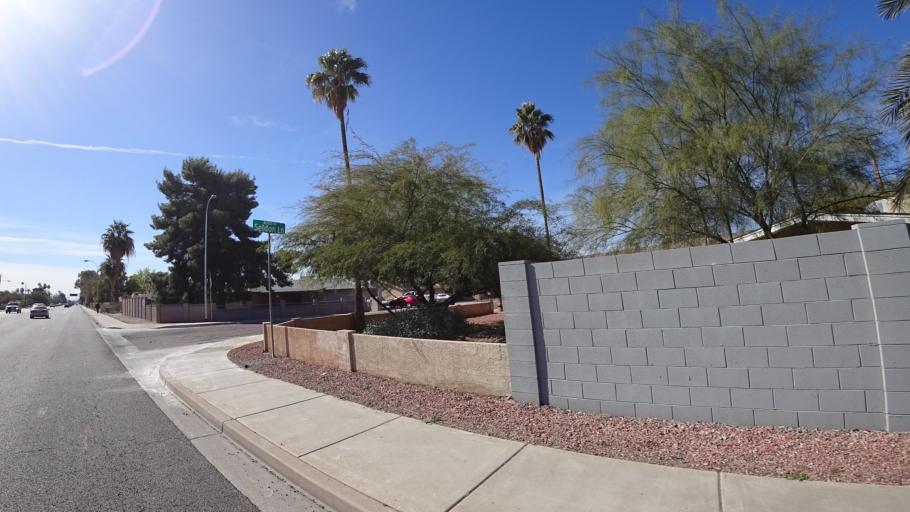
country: US
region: Arizona
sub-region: Maricopa County
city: Glendale
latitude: 33.5611
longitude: -112.1864
